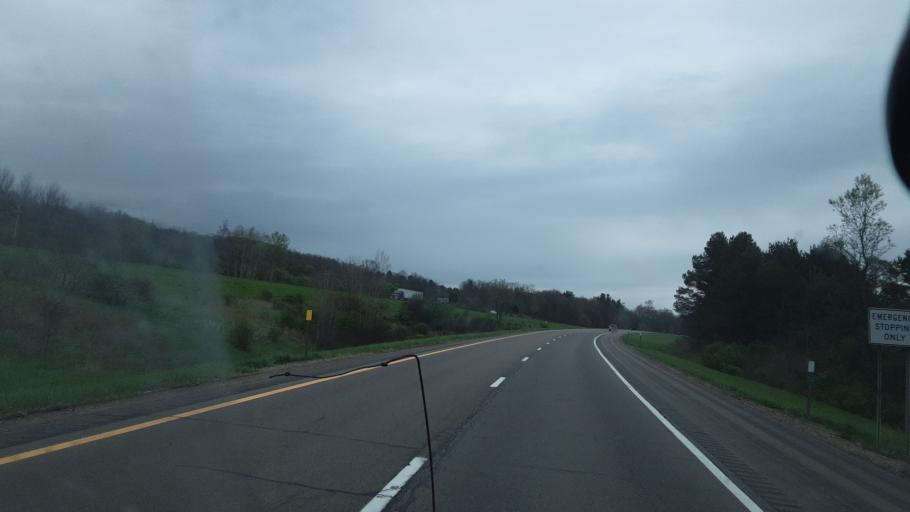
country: US
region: New York
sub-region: Allegany County
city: Friendship
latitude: 42.2172
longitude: -78.1354
